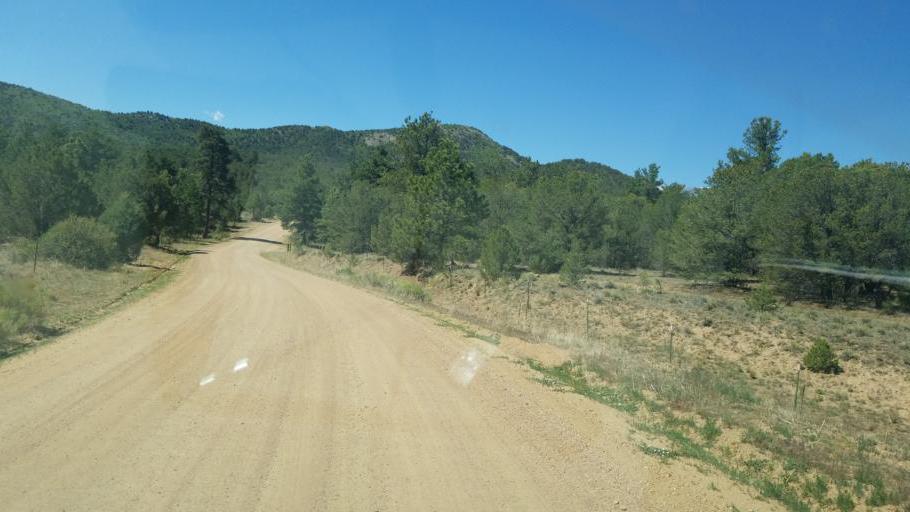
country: US
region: Colorado
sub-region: Custer County
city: Westcliffe
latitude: 38.2801
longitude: -105.5295
